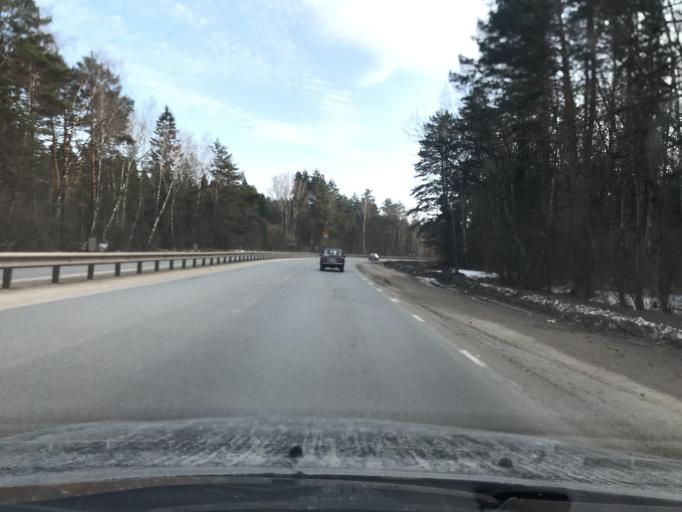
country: RU
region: Kaluga
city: Kaluga
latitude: 54.4556
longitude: 36.2377
